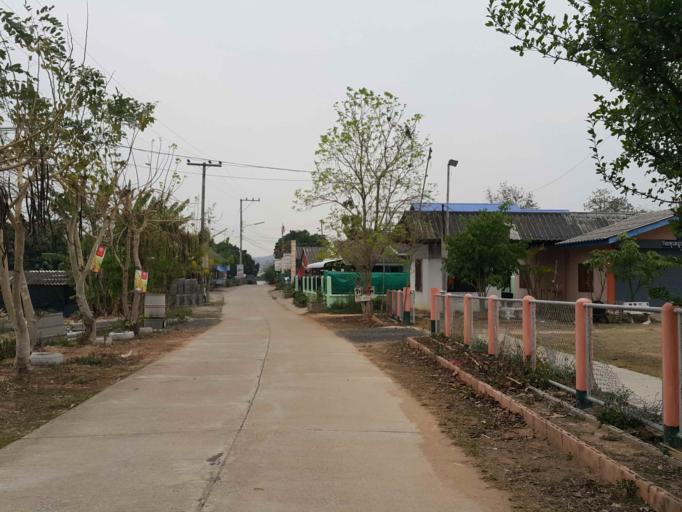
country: TH
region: Chiang Mai
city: Mae Taeng
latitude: 19.1027
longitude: 98.9997
